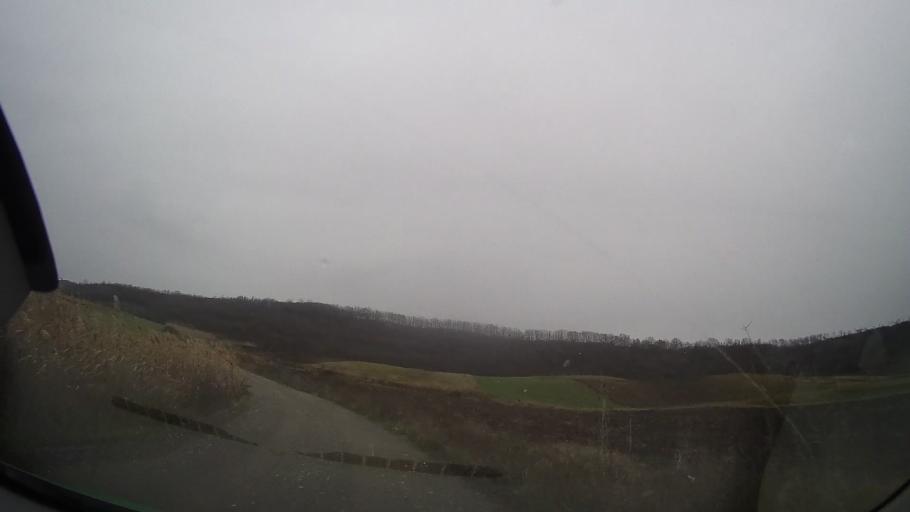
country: RO
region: Mures
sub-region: Comuna Ceausu de Campie
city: Ceausu de Campie
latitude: 46.6491
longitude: 24.4975
